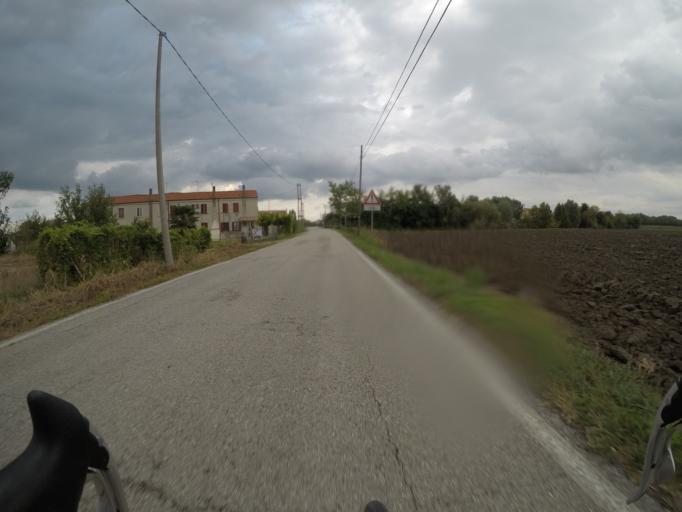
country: IT
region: Veneto
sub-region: Provincia di Rovigo
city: Arqua Polesine
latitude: 44.9911
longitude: 11.7273
